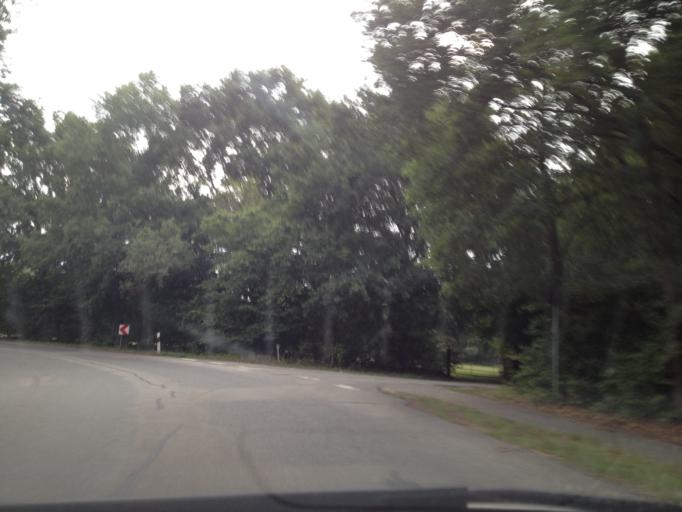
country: DE
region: Schleswig-Holstein
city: Daldorf
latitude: 54.0162
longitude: 10.2357
